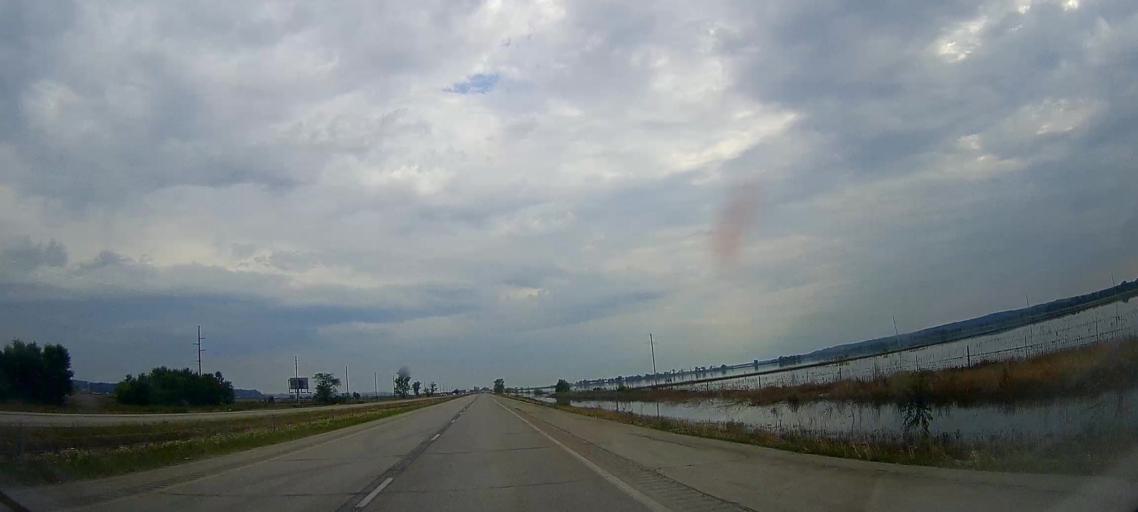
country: US
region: Iowa
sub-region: Harrison County
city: Missouri Valley
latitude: 41.4495
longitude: -95.8998
